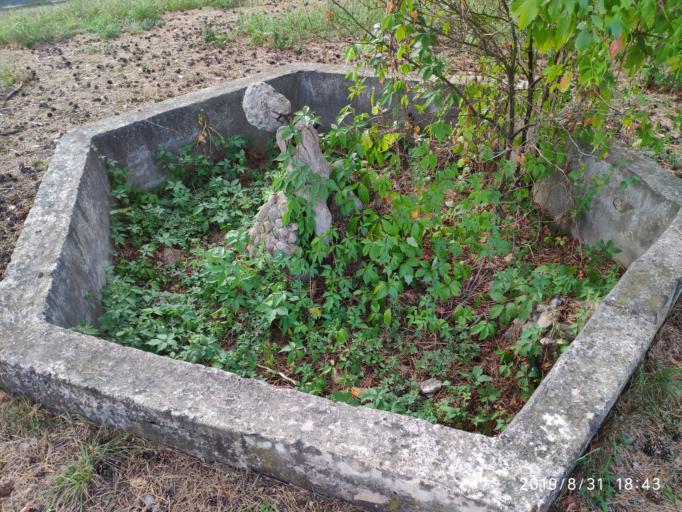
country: PL
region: Lubusz
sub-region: Powiat swiebodzinski
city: Sieniawa
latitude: 52.4091
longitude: 15.4747
